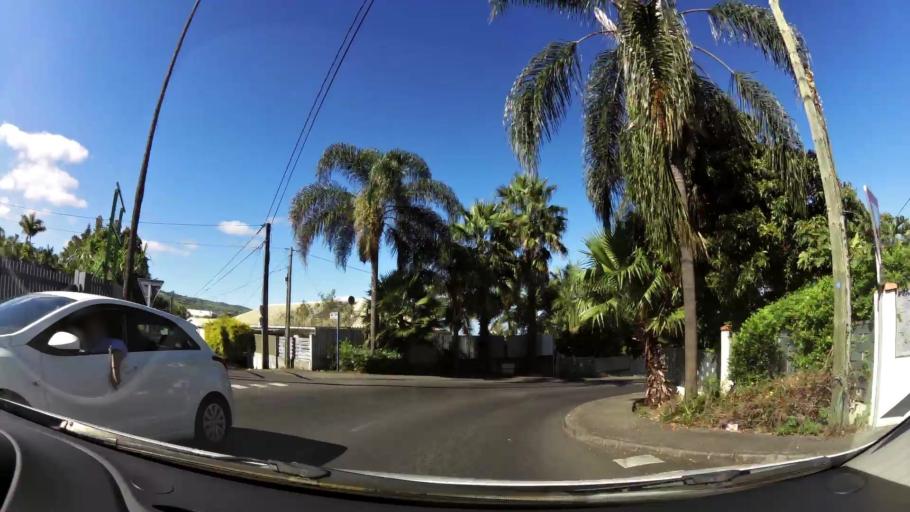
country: RE
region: Reunion
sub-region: Reunion
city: Le Tampon
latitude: -21.2770
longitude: 55.5247
